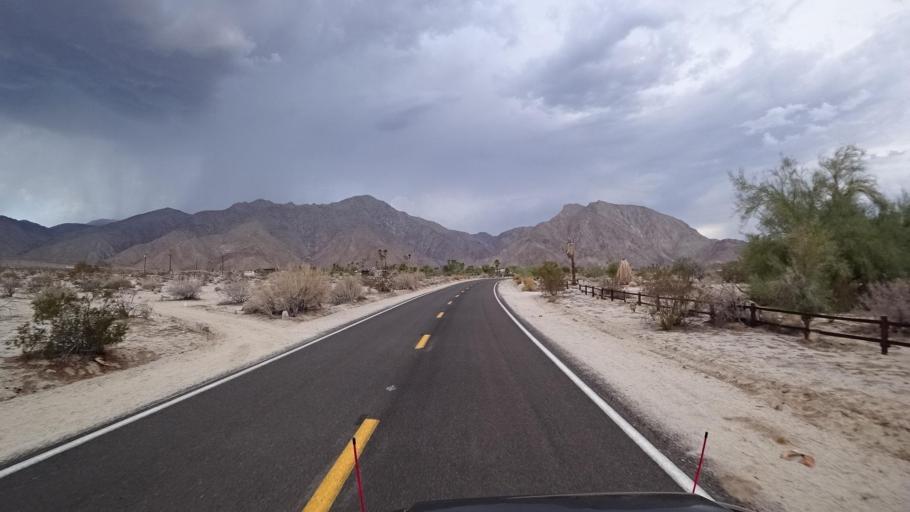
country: US
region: California
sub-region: San Diego County
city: Borrego Springs
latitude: 33.2596
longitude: -116.3933
